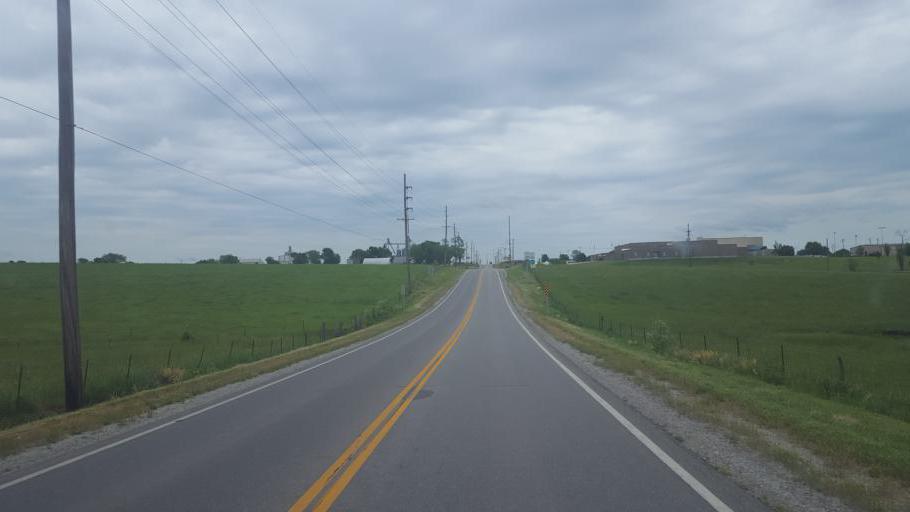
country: US
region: Missouri
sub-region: Moniteau County
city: California
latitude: 38.6358
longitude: -92.5979
